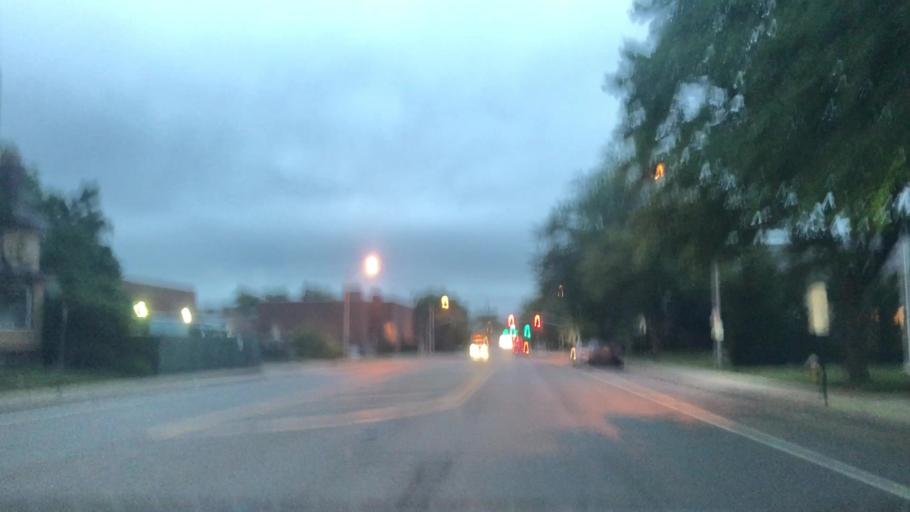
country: US
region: New York
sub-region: Nassau County
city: Rockville Centre
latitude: 40.6627
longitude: -73.6503
